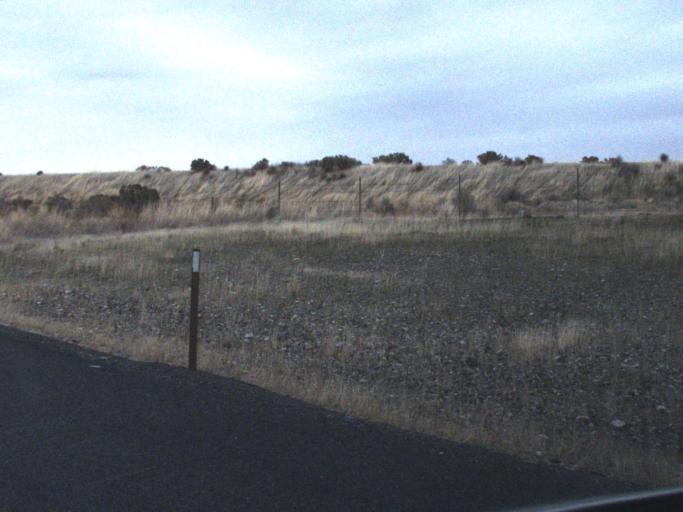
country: US
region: Washington
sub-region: Adams County
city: Ritzville
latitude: 46.7443
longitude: -118.2353
